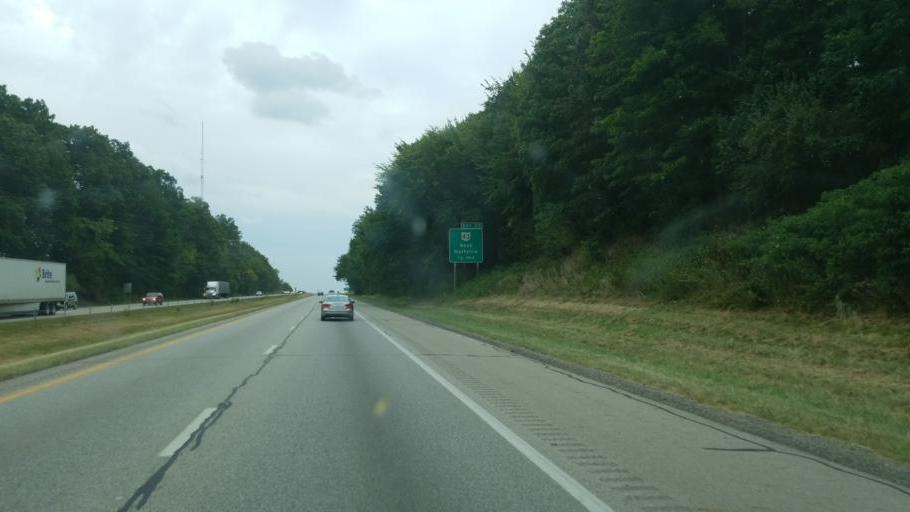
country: US
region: Ohio
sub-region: Portage County
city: Brimfield
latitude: 41.1066
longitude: -81.3614
